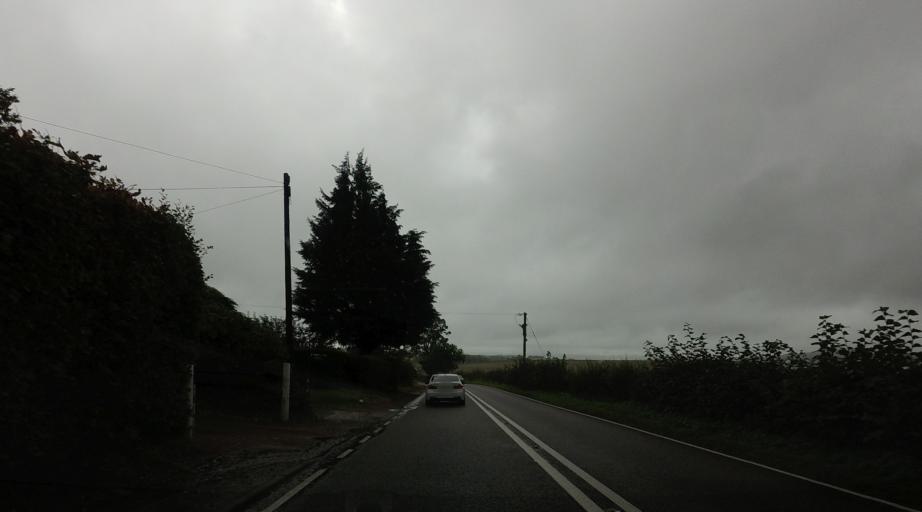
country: GB
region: Scotland
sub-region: Fife
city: Newport-On-Tay
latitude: 56.4233
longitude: -2.9220
